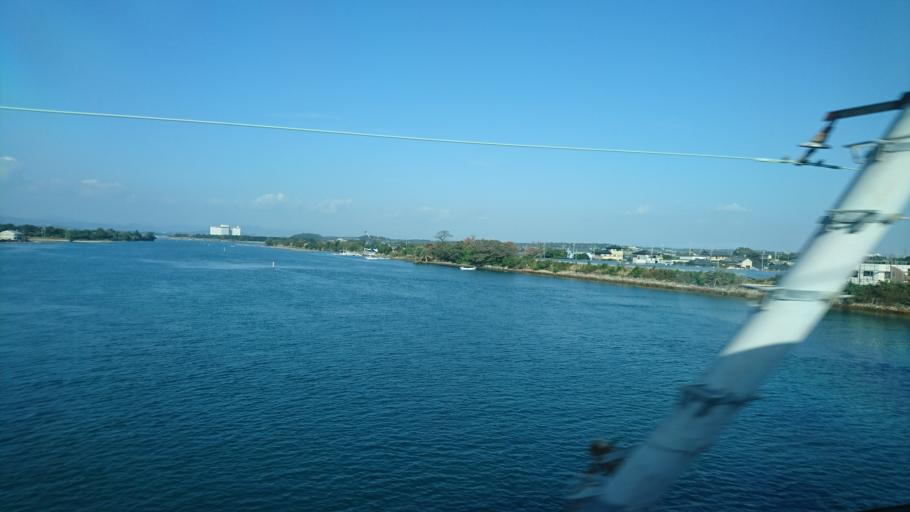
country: JP
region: Shizuoka
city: Kosai-shi
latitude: 34.6886
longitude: 137.6063
